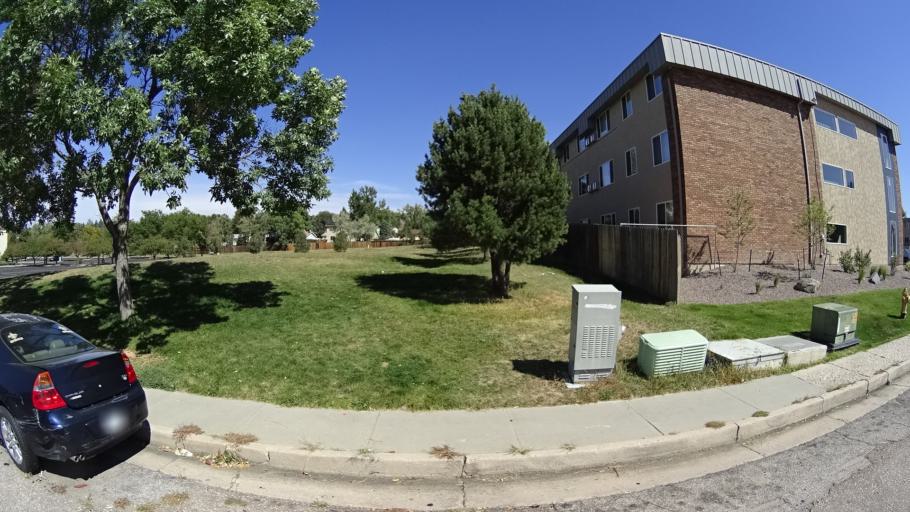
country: US
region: Colorado
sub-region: El Paso County
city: Cimarron Hills
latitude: 38.9035
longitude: -104.7695
